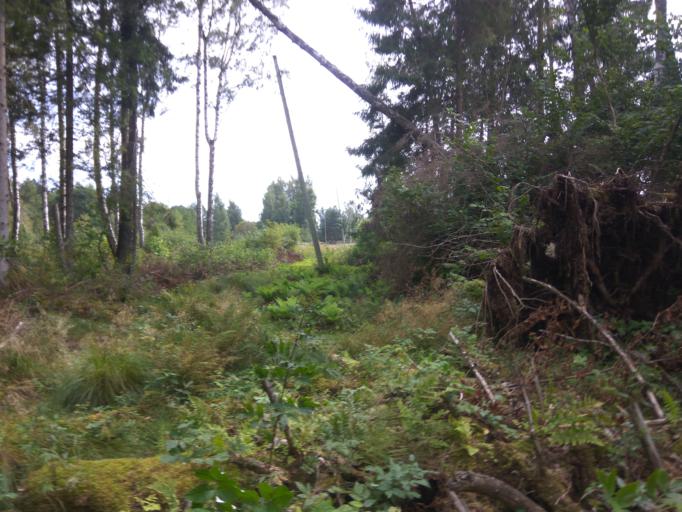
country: LV
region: Alsunga
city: Alsunga
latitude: 56.9827
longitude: 21.6868
